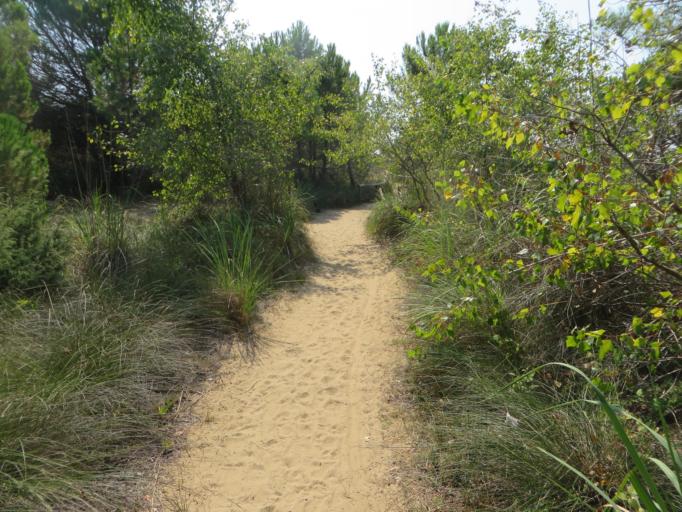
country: IT
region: Veneto
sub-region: Provincia di Venezia
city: Crepaldo
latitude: 45.5337
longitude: 12.7379
